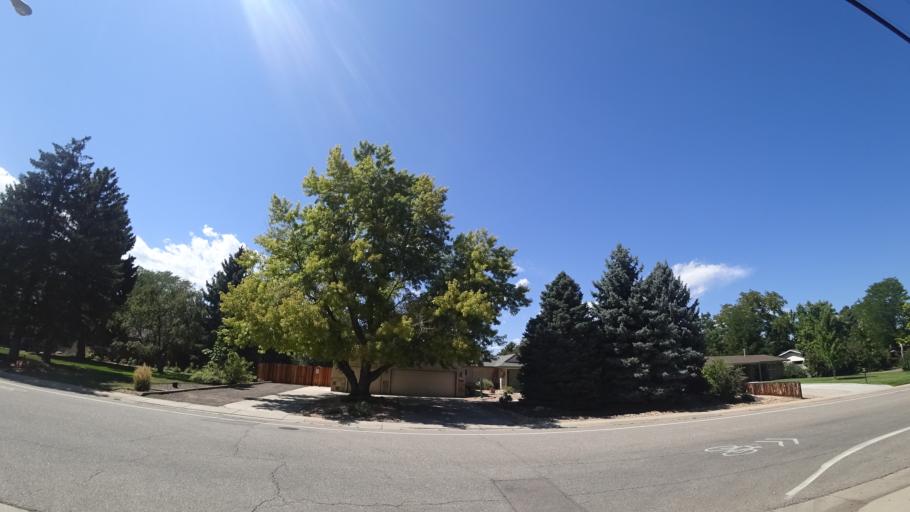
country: US
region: Colorado
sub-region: Arapahoe County
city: Greenwood Village
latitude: 39.6061
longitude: -104.9785
